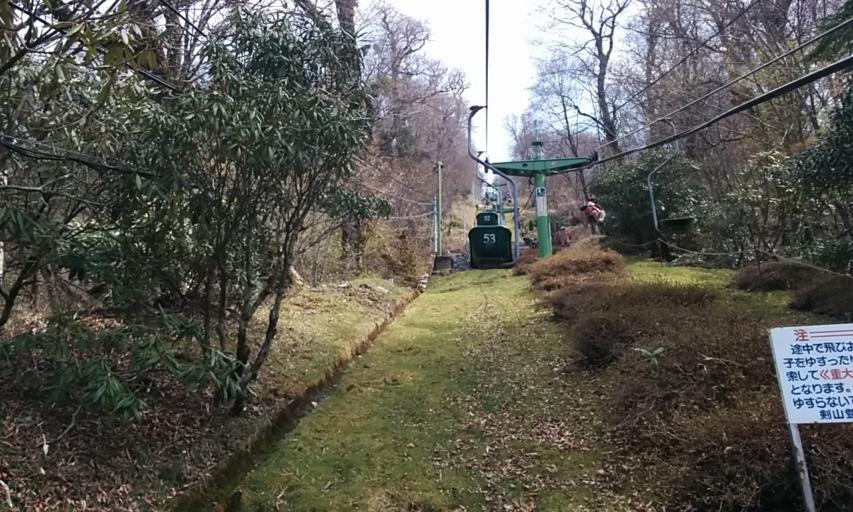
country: JP
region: Tokushima
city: Wakimachi
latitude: 33.8664
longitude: 134.0891
